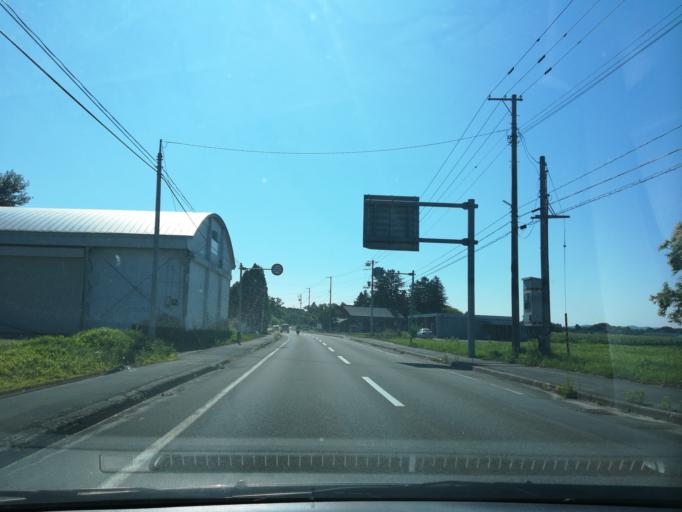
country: JP
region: Hokkaido
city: Chitose
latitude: 42.9153
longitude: 141.8937
